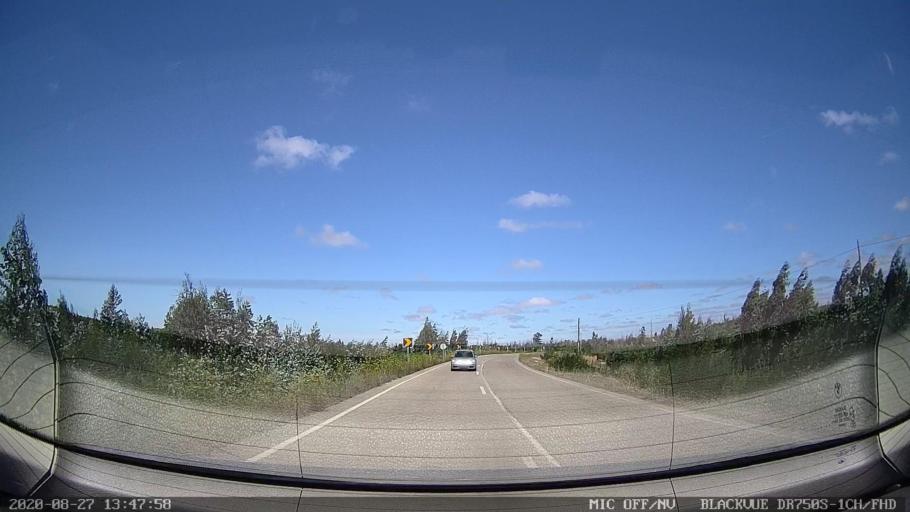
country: PT
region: Coimbra
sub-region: Mira
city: Mira
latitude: 40.3831
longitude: -8.7441
